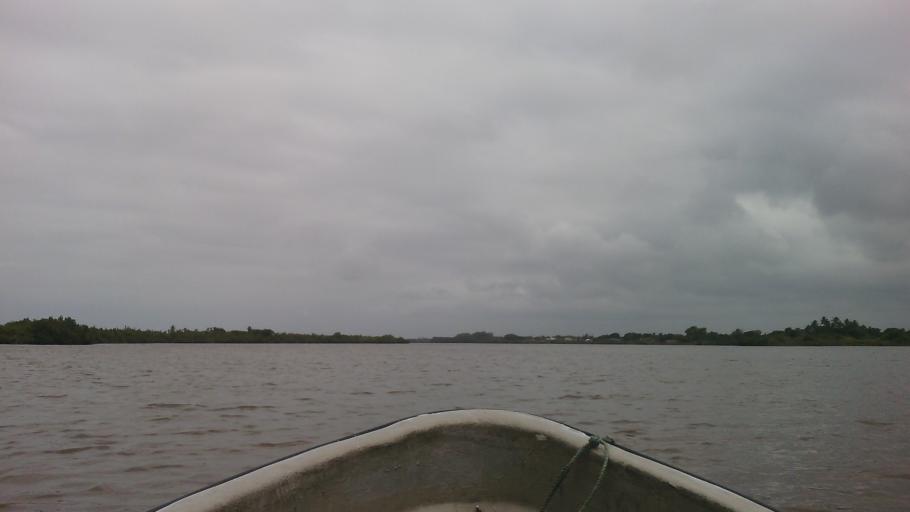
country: BJ
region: Atlantique
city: Hevie
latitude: 6.3506
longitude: 2.2829
